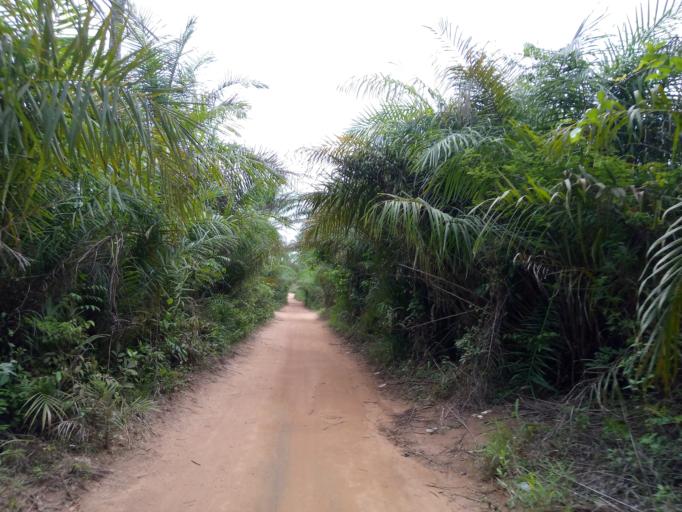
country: SL
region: Western Area
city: Waterloo
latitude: 8.3965
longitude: -12.9463
